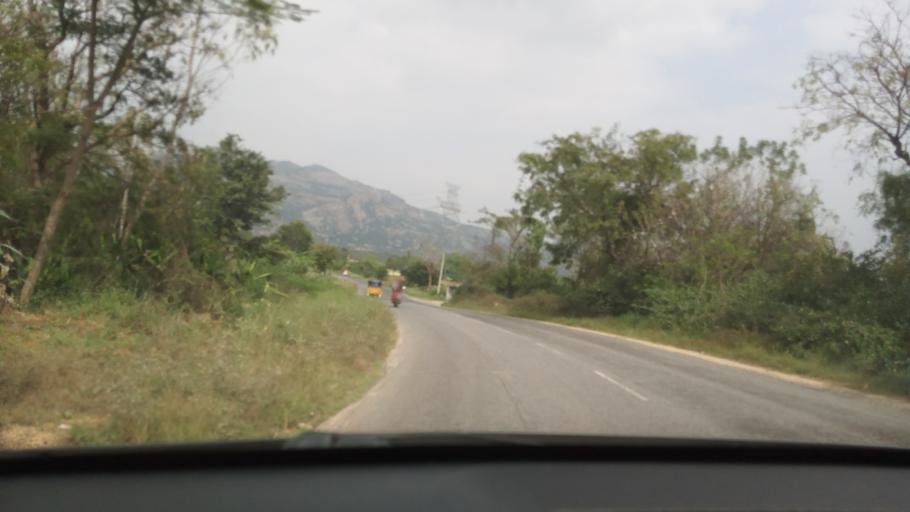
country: IN
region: Andhra Pradesh
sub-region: Chittoor
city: Madanapalle
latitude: 13.6531
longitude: 78.8345
